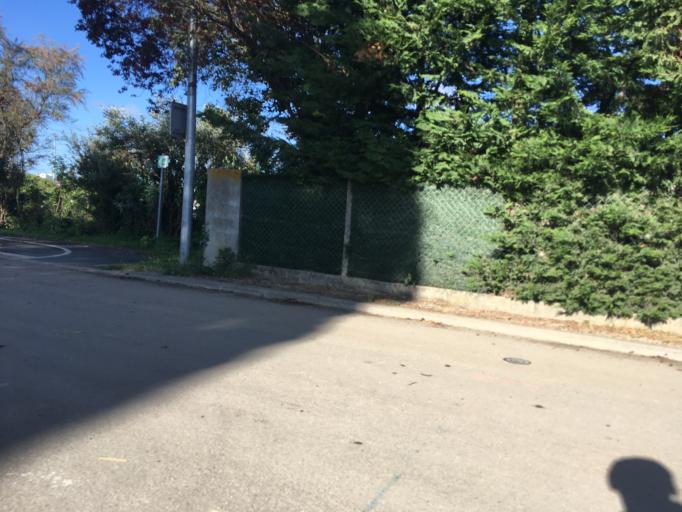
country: FR
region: Poitou-Charentes
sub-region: Departement de la Charente-Maritime
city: Lagord
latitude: 46.1755
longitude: -1.1749
